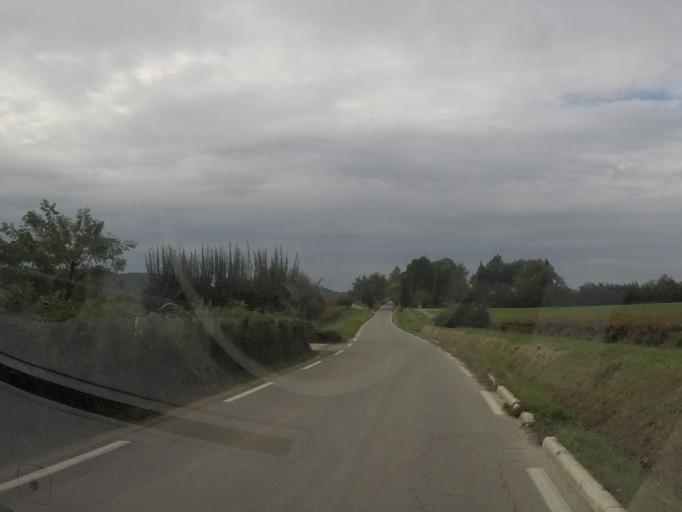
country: FR
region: Provence-Alpes-Cote d'Azur
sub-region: Departement du Vaucluse
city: Ansouis
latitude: 43.7427
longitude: 5.4522
